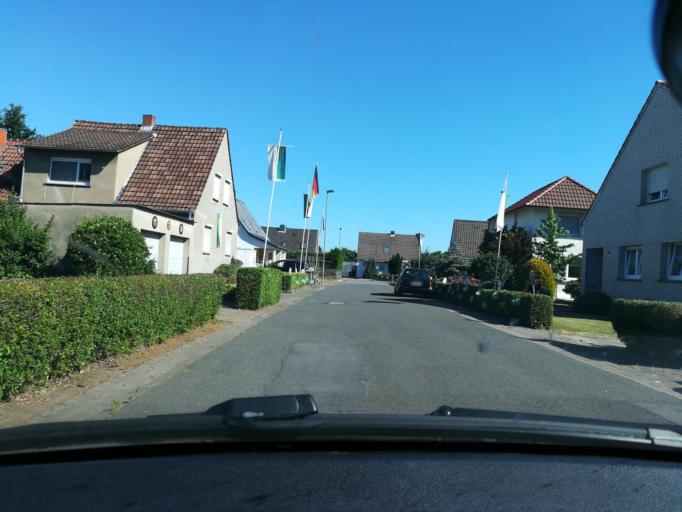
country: DE
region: North Rhine-Westphalia
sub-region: Regierungsbezirk Detmold
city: Minden
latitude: 52.3114
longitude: 8.9301
